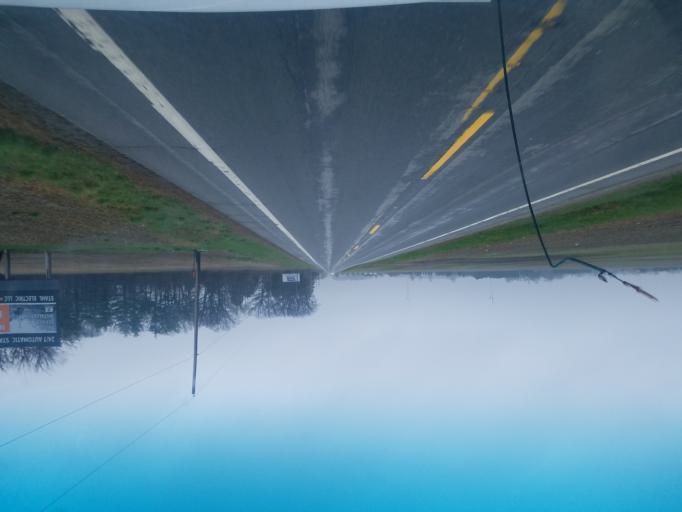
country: US
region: Ohio
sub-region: Wood County
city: Weston
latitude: 41.3722
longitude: -83.7596
